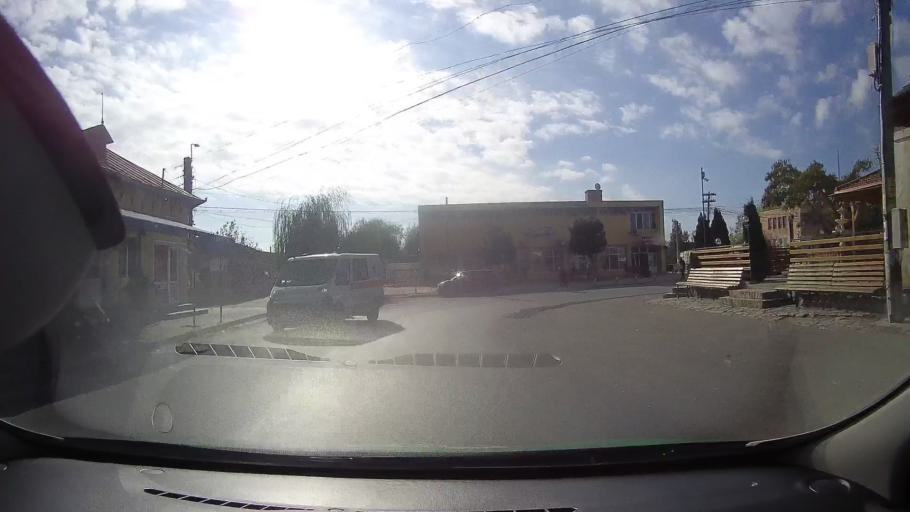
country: RO
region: Tulcea
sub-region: Comuna Sarichioi
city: Sarichioi
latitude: 44.9434
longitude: 28.8538
